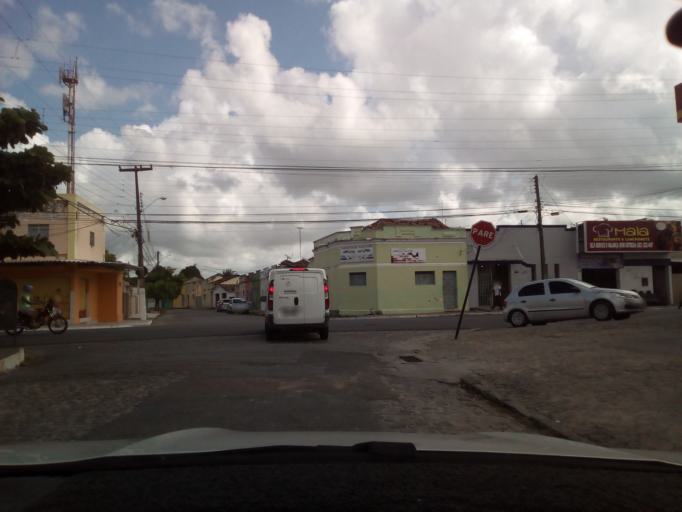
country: BR
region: Paraiba
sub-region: Joao Pessoa
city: Joao Pessoa
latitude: -7.1335
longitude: -34.8759
